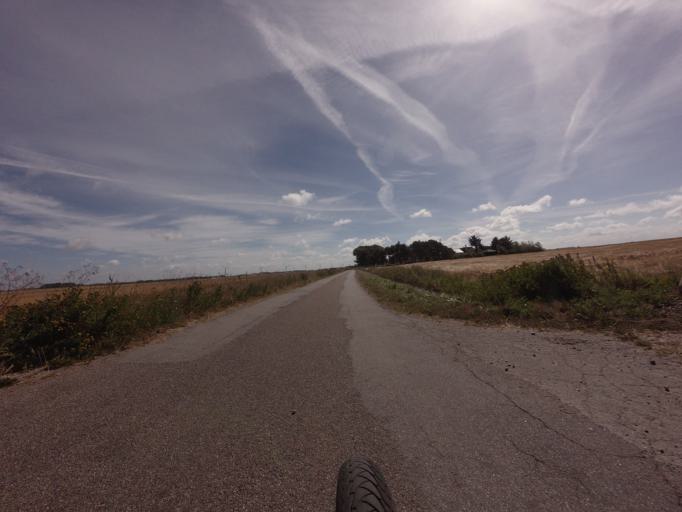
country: DK
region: North Denmark
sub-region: Hjorring Kommune
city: Vra
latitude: 57.3424
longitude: 9.7953
